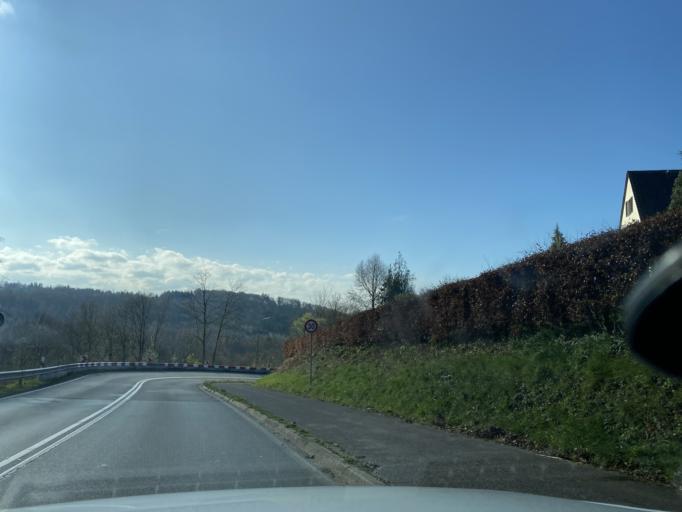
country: DE
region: North Rhine-Westphalia
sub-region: Regierungsbezirk Koln
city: Odenthal
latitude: 51.0563
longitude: 7.1281
